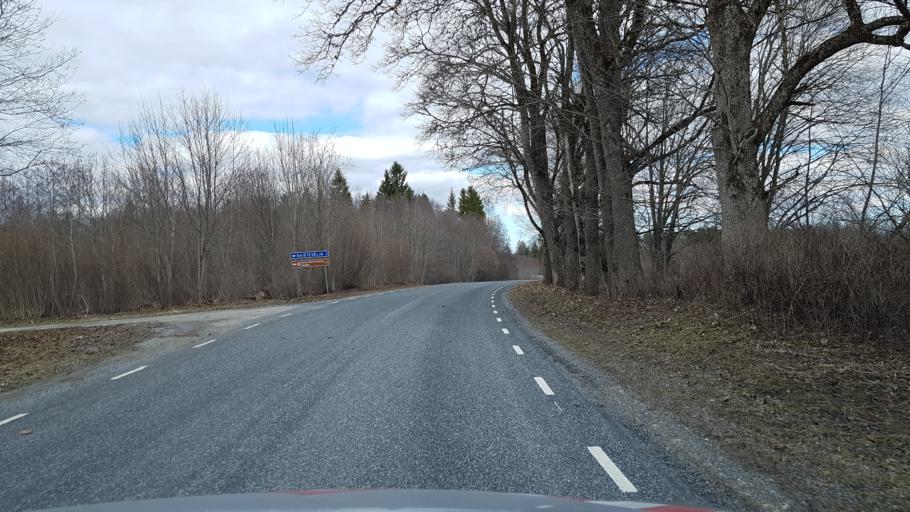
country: EE
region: Laeaene-Virumaa
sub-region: Tamsalu vald
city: Tamsalu
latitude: 59.1841
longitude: 26.1278
